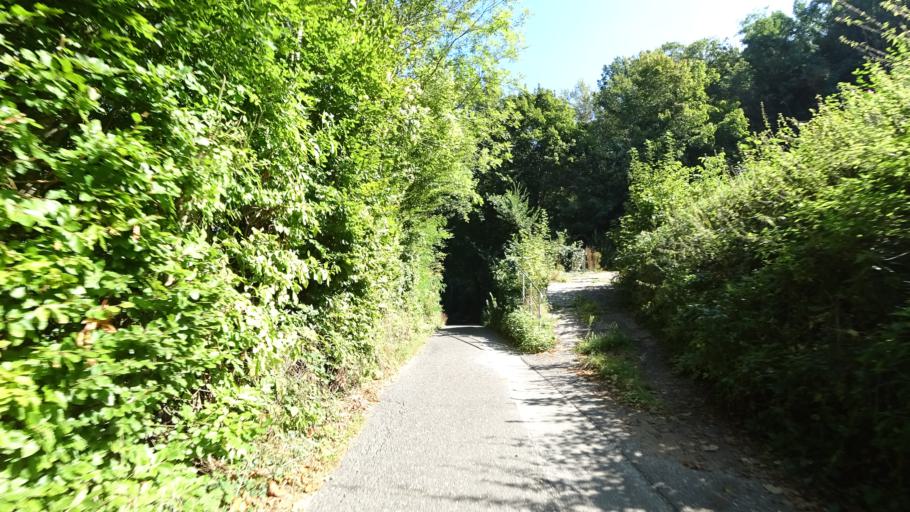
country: DE
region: Bavaria
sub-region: Regierungsbezirk Unterfranken
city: Miltenberg
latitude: 49.6970
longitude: 9.2556
